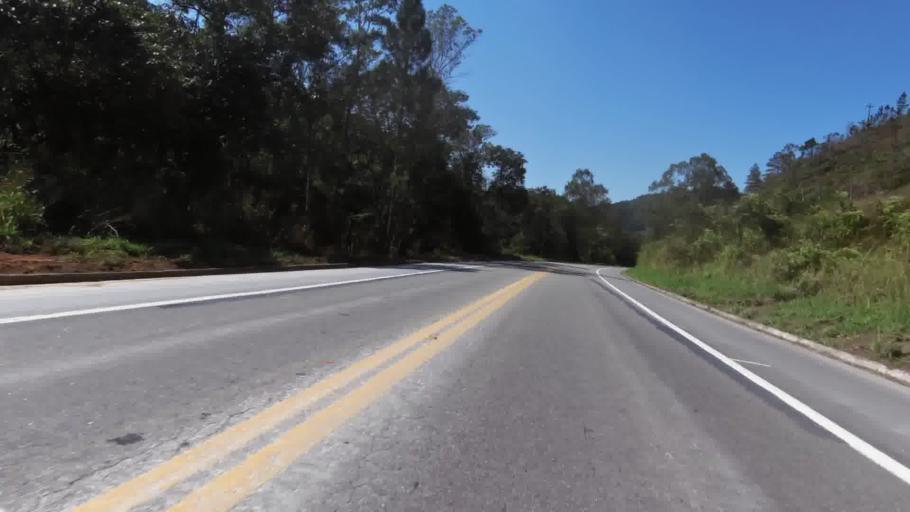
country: BR
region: Espirito Santo
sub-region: Marechal Floriano
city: Marechal Floriano
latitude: -20.4132
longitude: -40.8524
